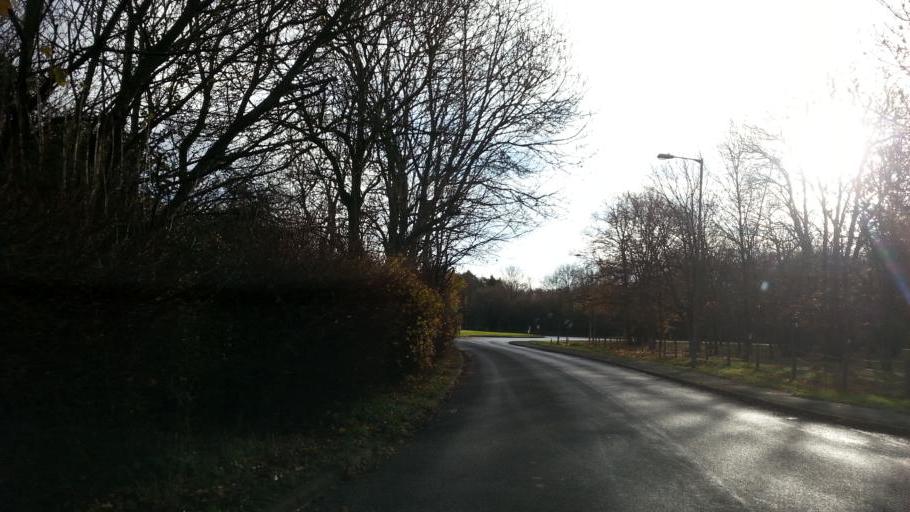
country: GB
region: England
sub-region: Suffolk
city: Wickham Market
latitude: 52.1308
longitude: 1.4232
